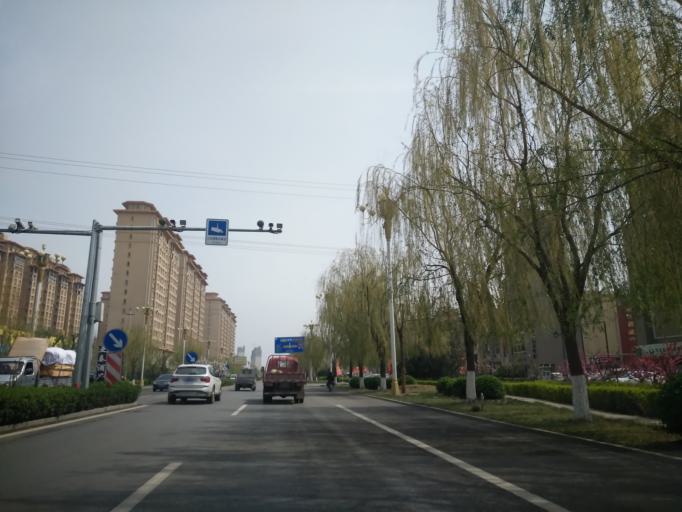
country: CN
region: Beijing
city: Xiji
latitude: 39.7456
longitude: 116.9806
